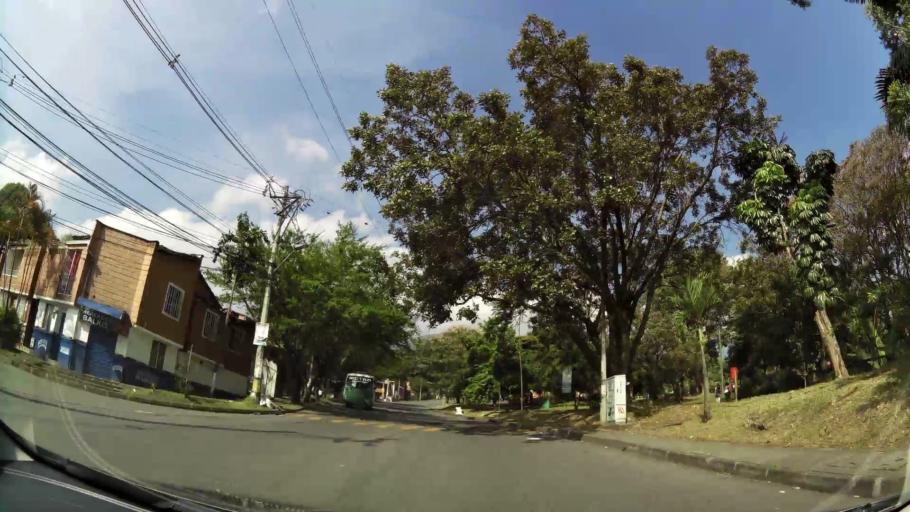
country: CO
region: Antioquia
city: La Estrella
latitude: 6.1683
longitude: -75.6412
